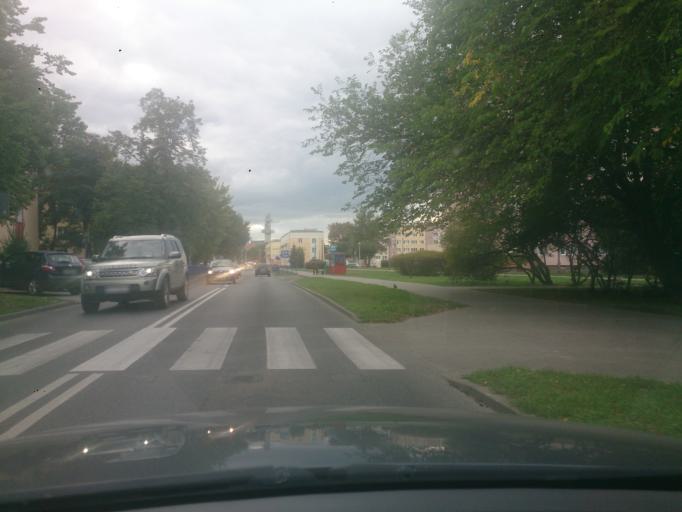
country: PL
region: Kujawsko-Pomorskie
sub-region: Grudziadz
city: Grudziadz
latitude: 53.4769
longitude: 18.7542
